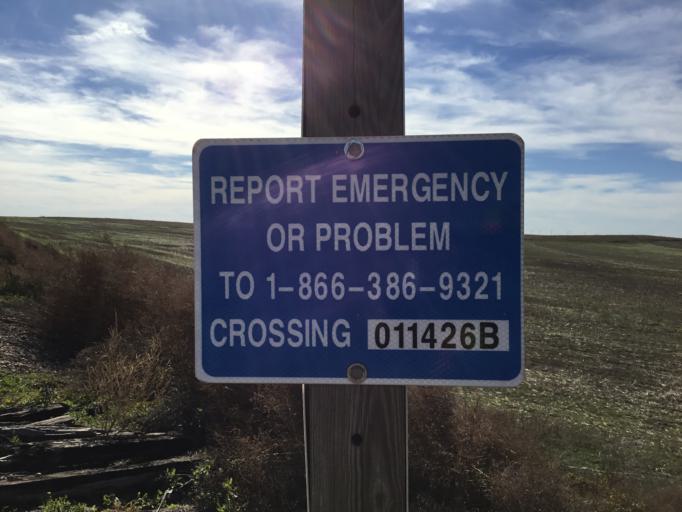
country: US
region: Kansas
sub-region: Lincoln County
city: Lincoln
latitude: 38.9726
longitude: -98.0482
